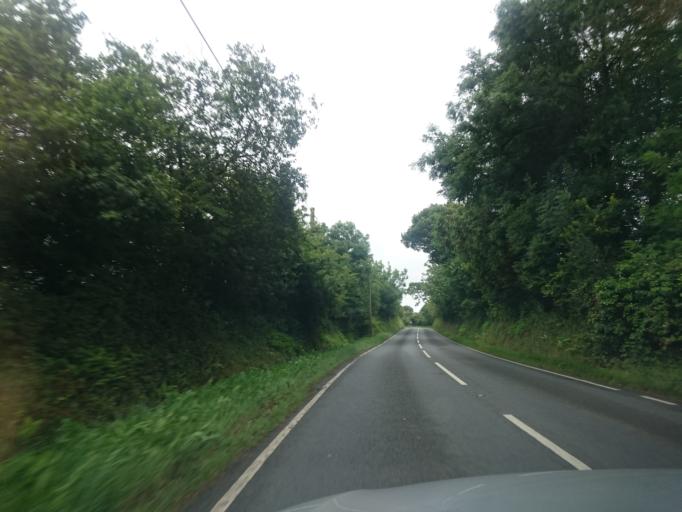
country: GB
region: Wales
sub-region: Pembrokeshire
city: Freystrop
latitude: 51.7764
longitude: -4.9670
